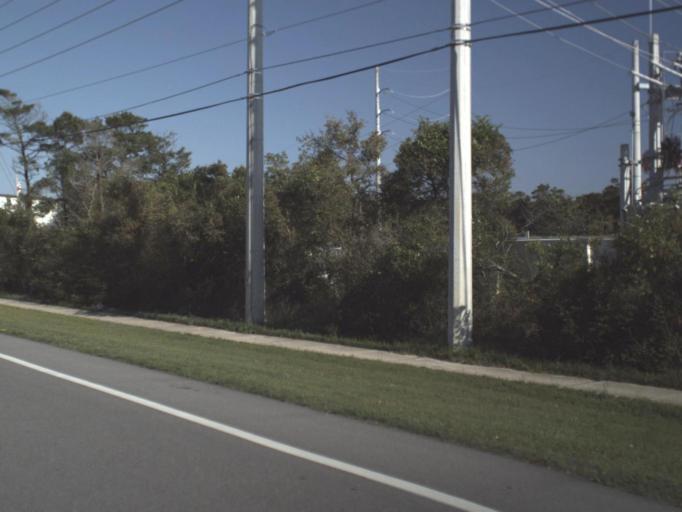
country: US
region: Florida
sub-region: Okaloosa County
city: Destin
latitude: 30.3874
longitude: -86.4343
